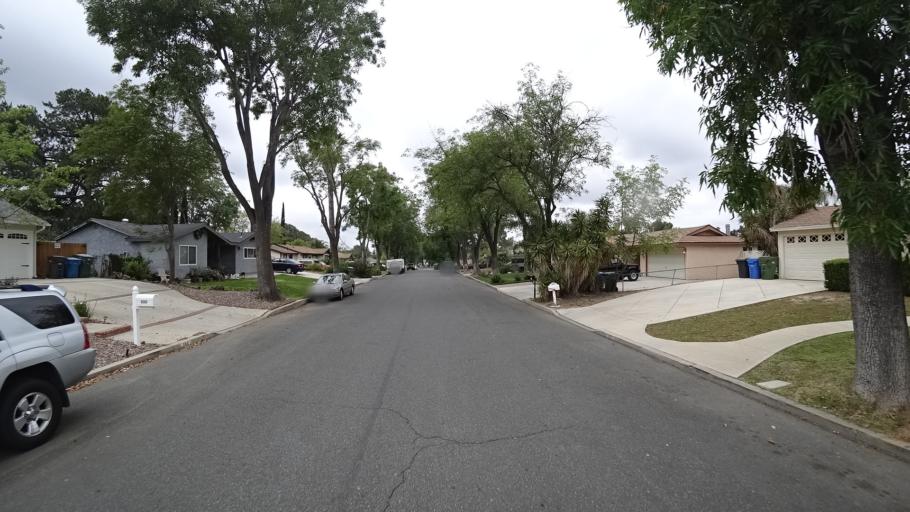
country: US
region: California
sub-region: Ventura County
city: Thousand Oaks
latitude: 34.2135
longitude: -118.8630
